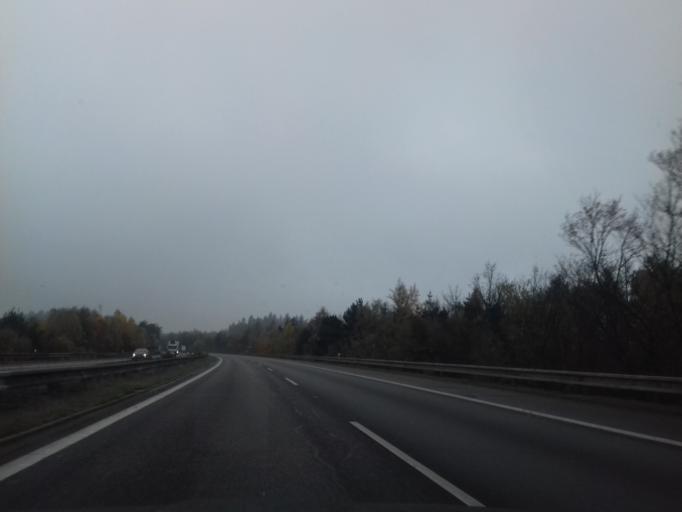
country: CZ
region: Vysocina
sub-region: Okres Pelhrimov
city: Humpolec
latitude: 49.5587
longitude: 15.3181
